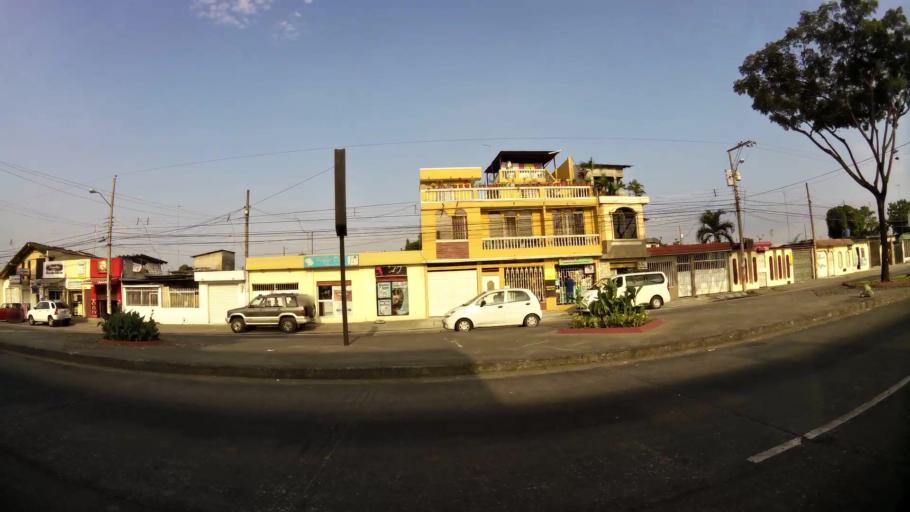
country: EC
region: Guayas
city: Eloy Alfaro
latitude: -2.1295
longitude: -79.9019
